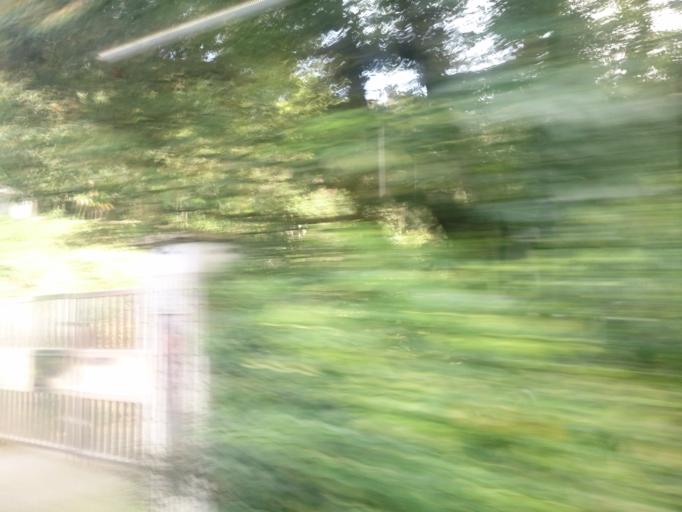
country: TW
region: Taipei
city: Taipei
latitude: 25.1625
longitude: 121.5444
